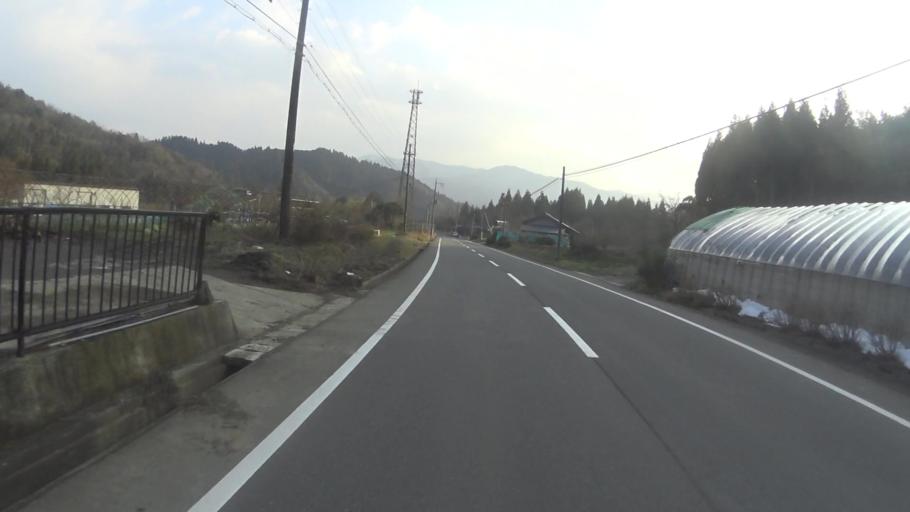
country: JP
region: Kyoto
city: Maizuru
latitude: 35.3839
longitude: 135.4176
